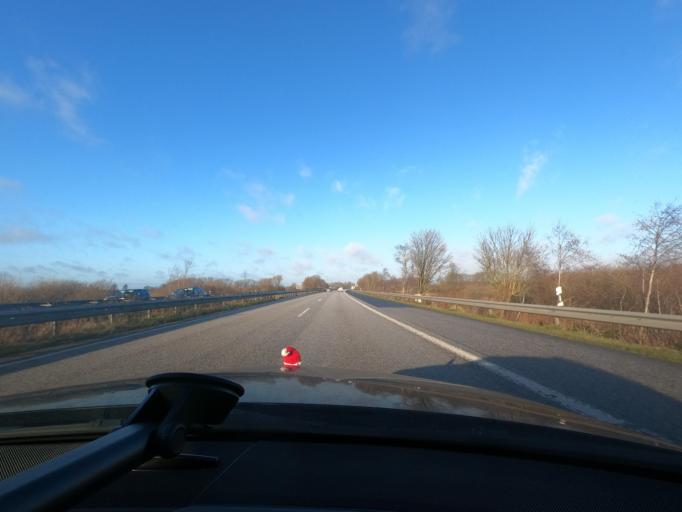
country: DE
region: Schleswig-Holstein
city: Schuby
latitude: 54.5417
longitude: 9.4703
